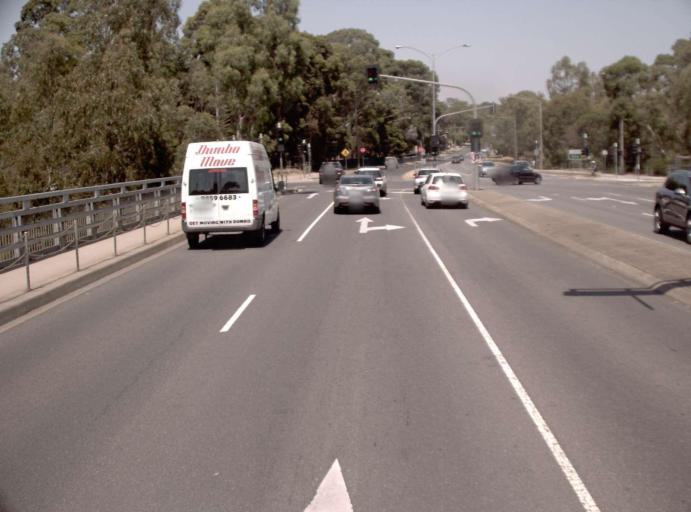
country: AU
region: Victoria
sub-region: Manningham
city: Bulleen
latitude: -37.7802
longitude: 145.0787
